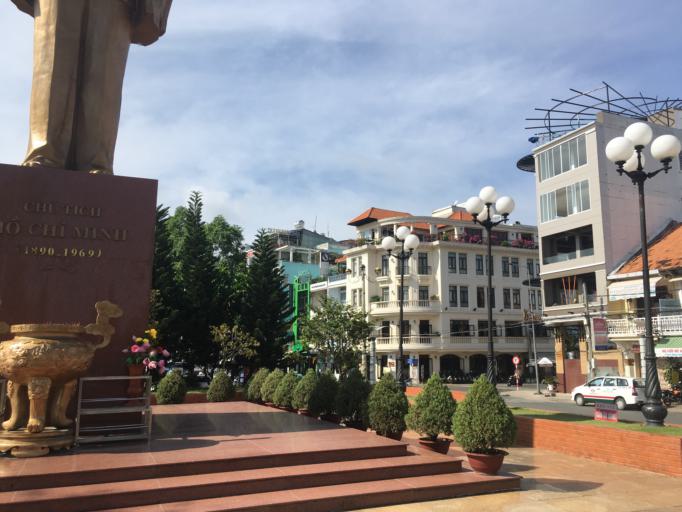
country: VN
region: Can Tho
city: Can Tho
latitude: 10.0339
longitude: 105.7887
